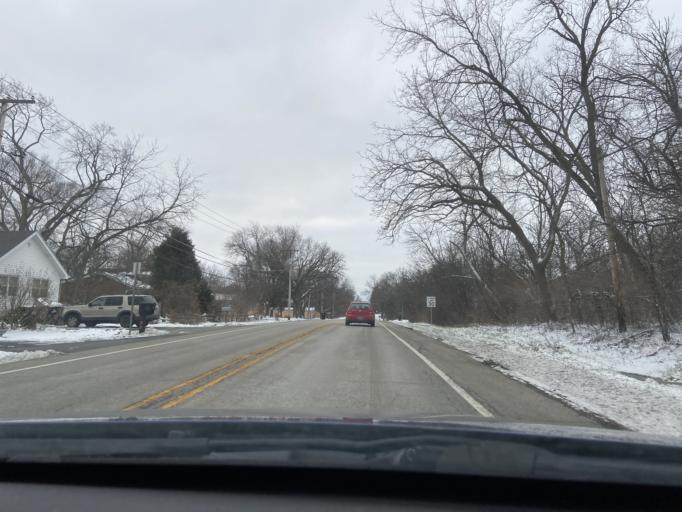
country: US
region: Illinois
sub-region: Lake County
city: Round Lake Park
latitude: 42.3641
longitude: -88.0680
